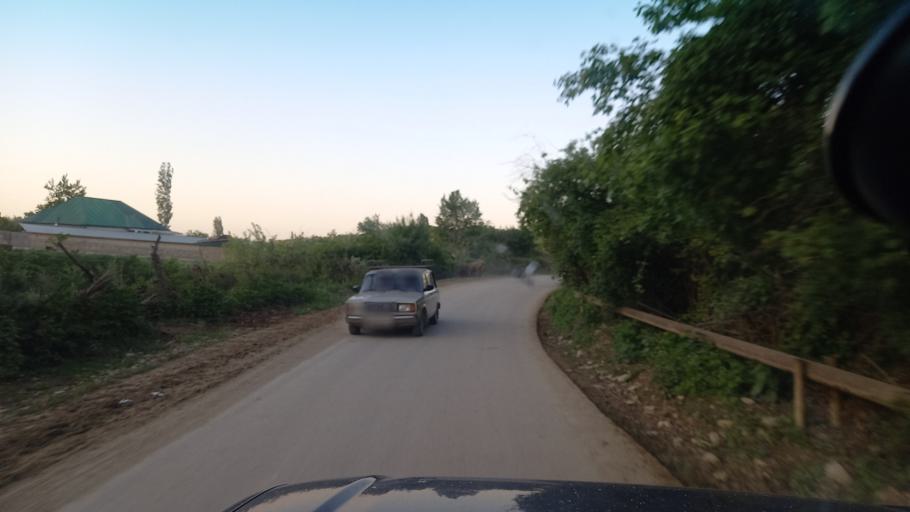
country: RU
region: Dagestan
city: Khuchni
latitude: 42.0312
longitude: 47.9699
